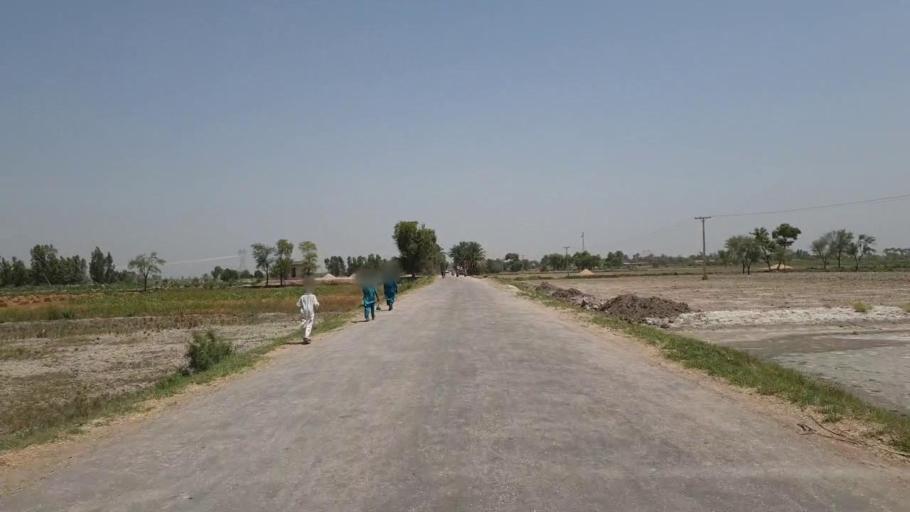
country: PK
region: Sindh
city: Adilpur
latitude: 27.8848
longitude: 69.2878
